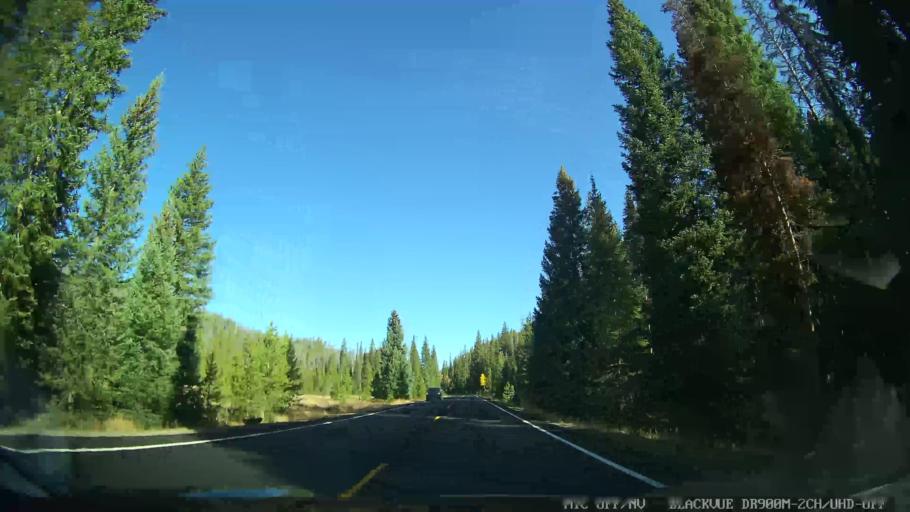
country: US
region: Colorado
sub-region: Grand County
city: Granby
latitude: 40.2959
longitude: -105.8427
